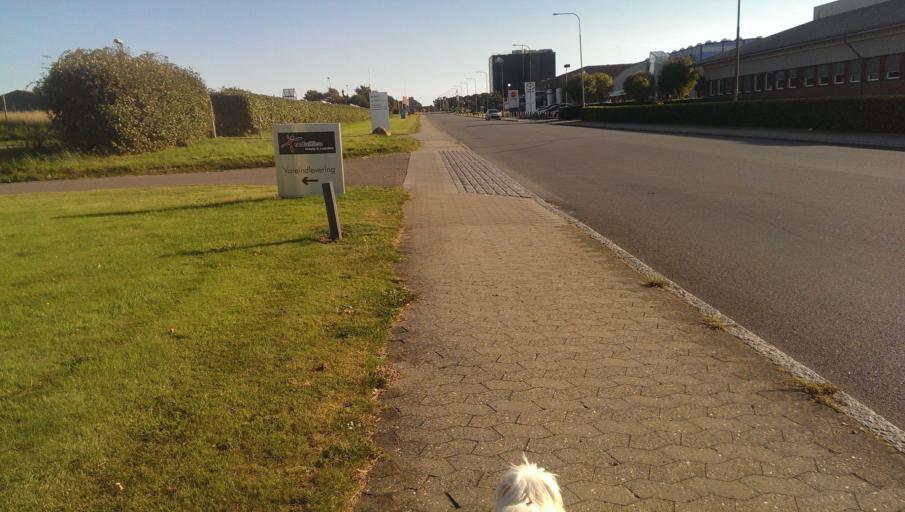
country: DK
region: South Denmark
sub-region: Esbjerg Kommune
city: Esbjerg
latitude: 55.4913
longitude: 8.4749
